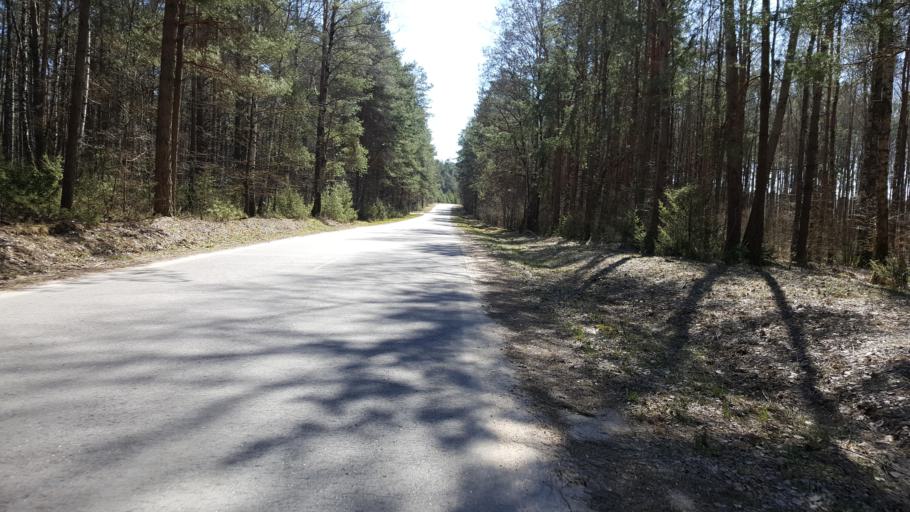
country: BY
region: Brest
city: Kamyanyets
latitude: 52.3604
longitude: 23.8168
